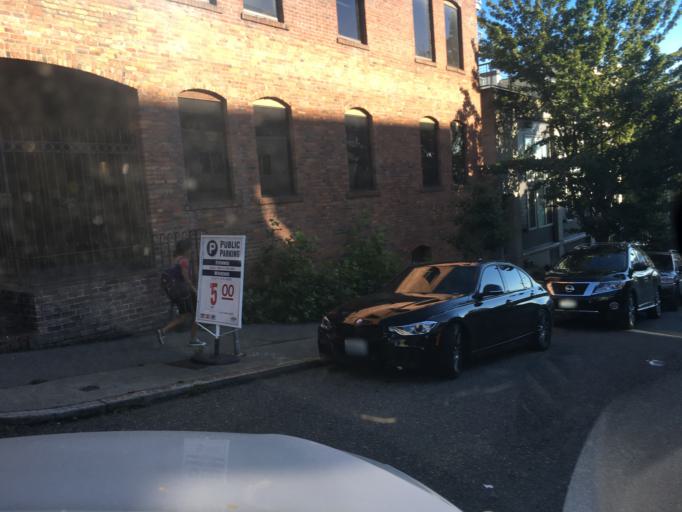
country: US
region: Washington
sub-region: King County
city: Seattle
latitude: 47.6144
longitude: -122.3491
